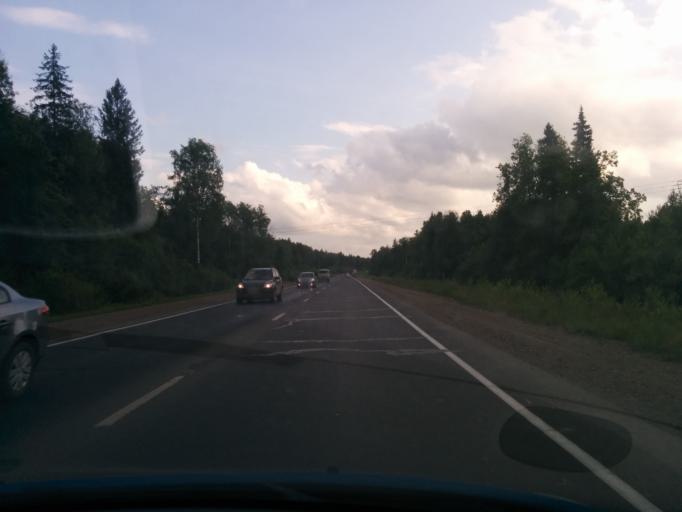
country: RU
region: Perm
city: Novyye Lyady
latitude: 58.0776
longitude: 56.4313
